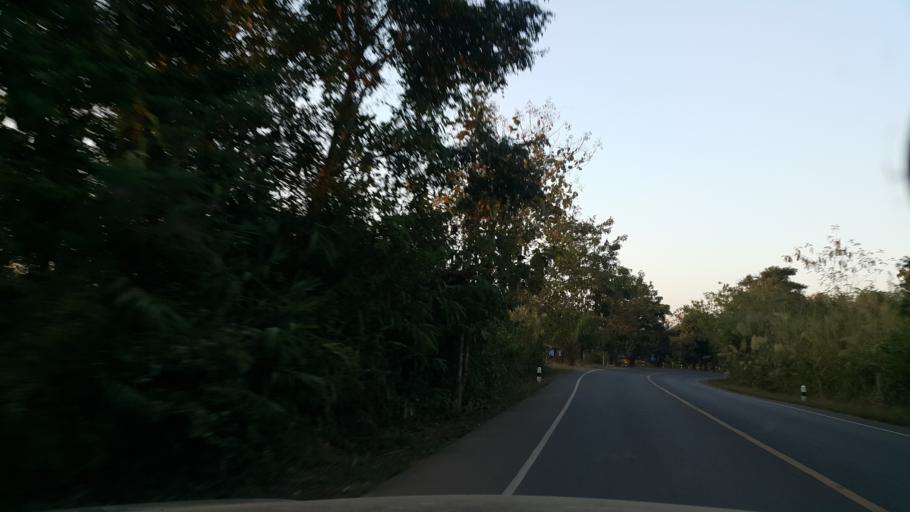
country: TH
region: Phrae
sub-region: Amphoe Wang Chin
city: Wang Chin
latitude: 17.8501
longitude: 99.6278
